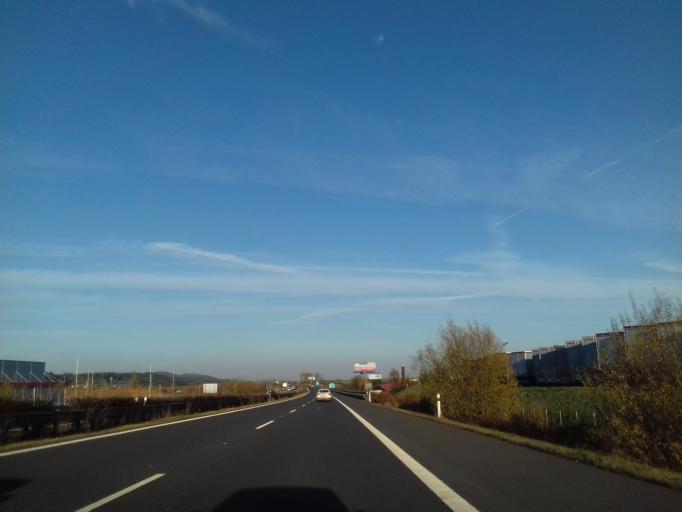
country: CZ
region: Central Bohemia
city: Zebrak
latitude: 49.8637
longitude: 13.8903
